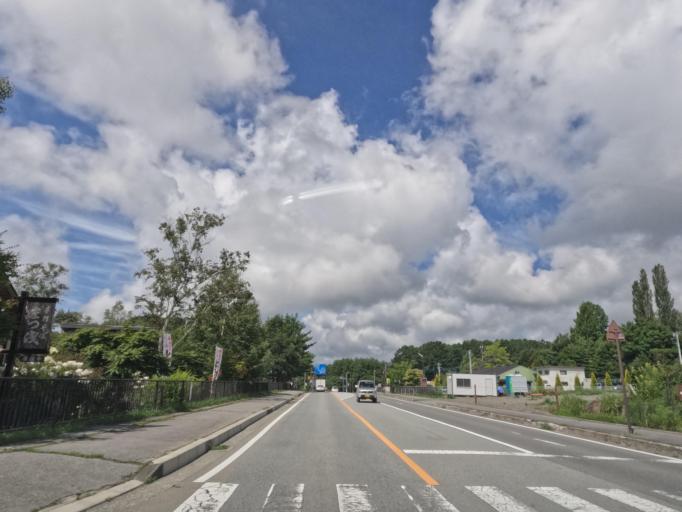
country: JP
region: Yamanashi
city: Nirasaki
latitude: 35.8868
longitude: 138.4136
